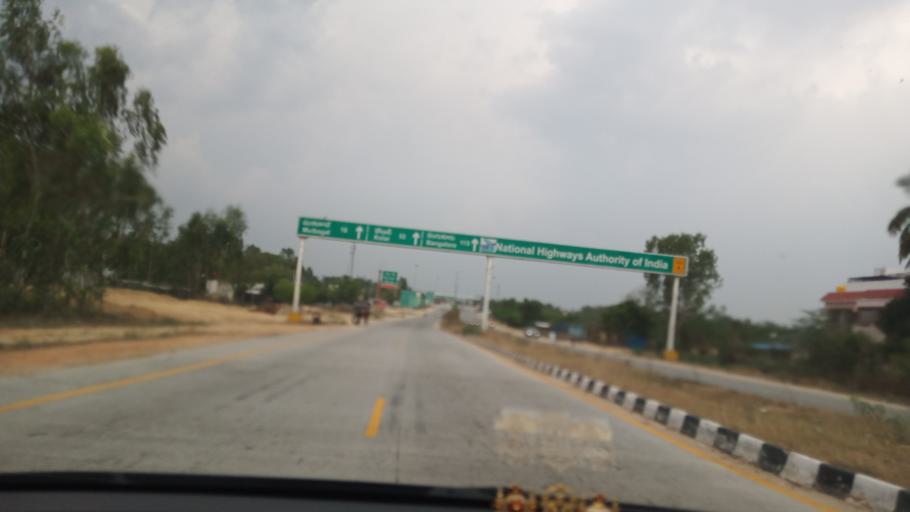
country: IN
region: Karnataka
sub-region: Kolar
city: Mulbagal
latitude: 13.1940
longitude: 78.5509
